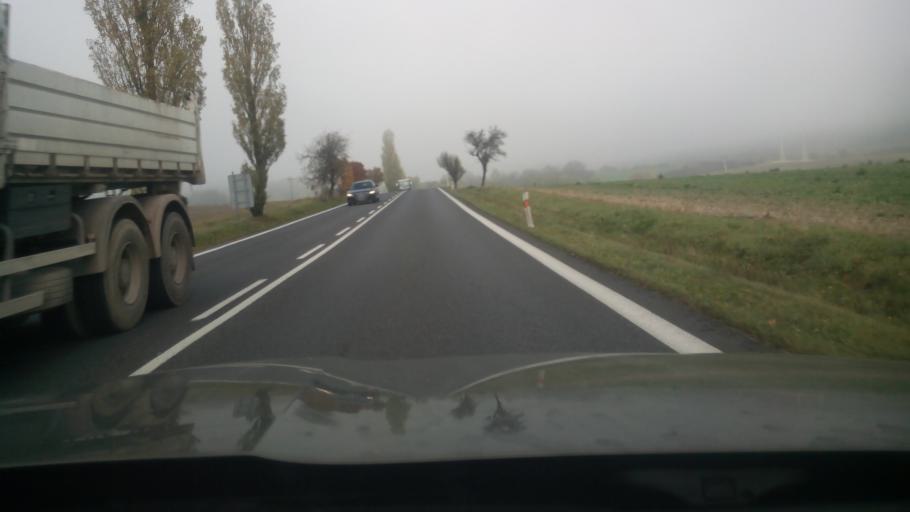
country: CZ
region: Central Bohemia
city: Milin
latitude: 49.6127
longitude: 14.0574
